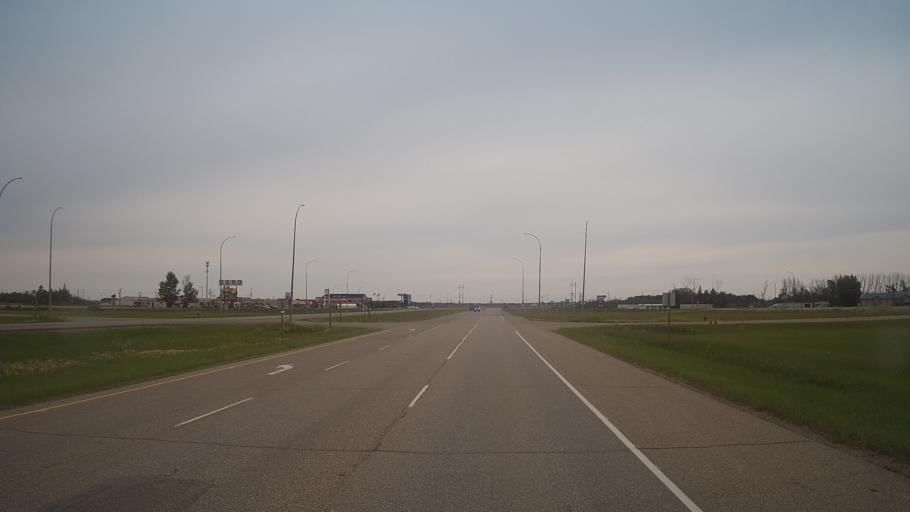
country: CA
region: Saskatchewan
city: Saskatoon
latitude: 52.0530
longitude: -106.5968
